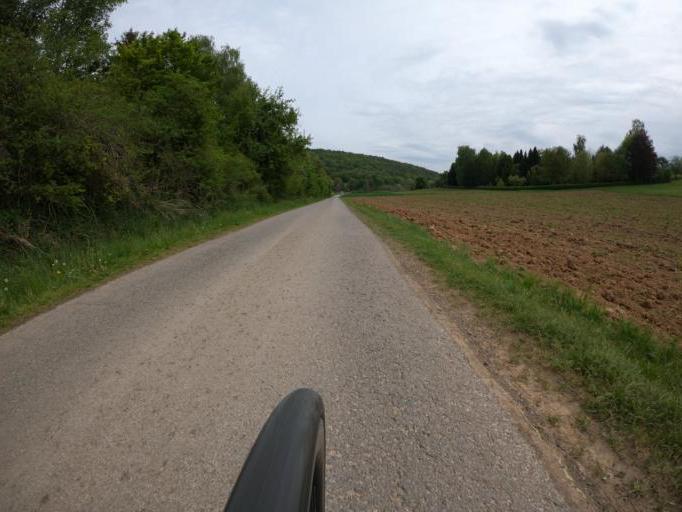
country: DE
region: Baden-Wuerttemberg
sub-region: Regierungsbezirk Stuttgart
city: Aidlingen
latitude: 48.6852
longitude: 8.8971
